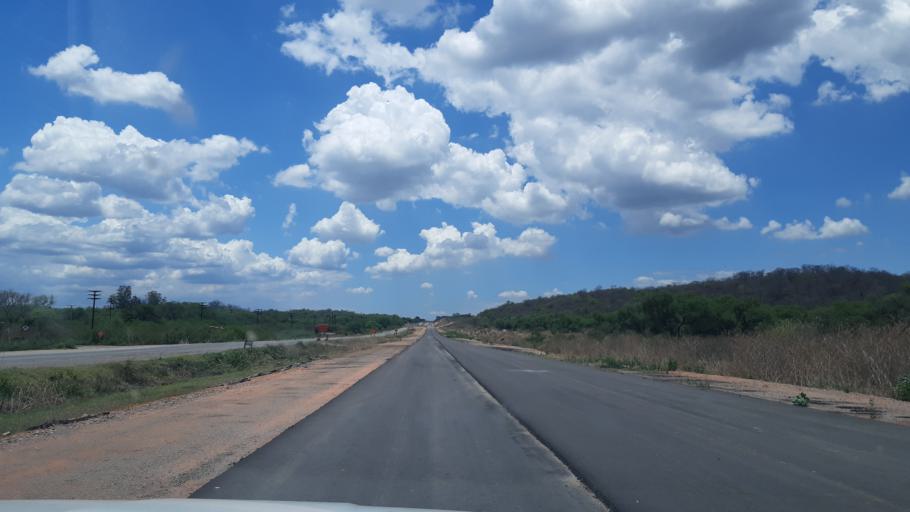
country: AR
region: Jujuy
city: La Mendieta
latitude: -24.4295
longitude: -65.0067
